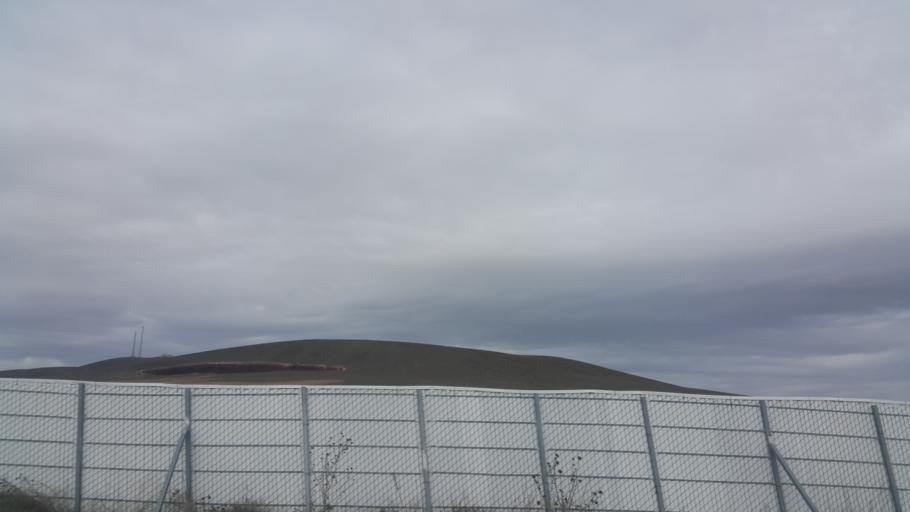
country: TR
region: Aksaray
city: Taspinar
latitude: 37.9408
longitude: 34.0964
